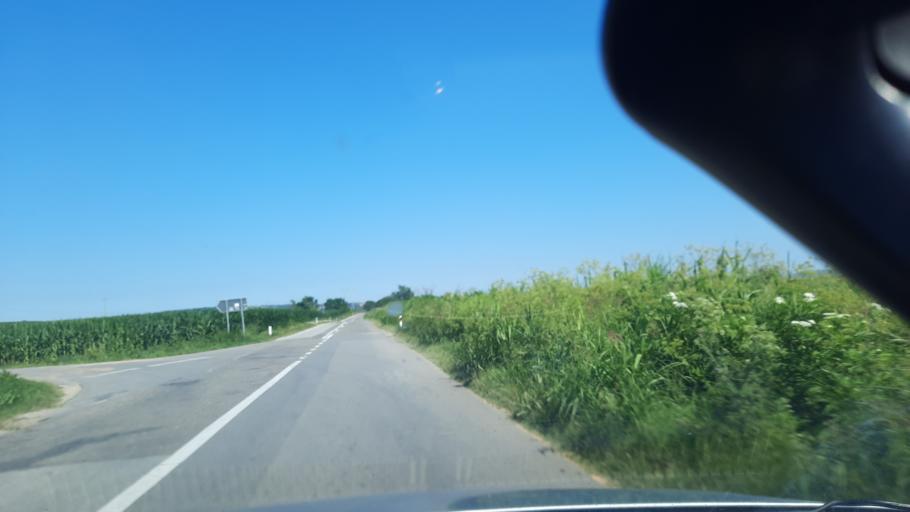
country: RS
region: Central Serbia
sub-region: Branicevski Okrug
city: Malo Crnice
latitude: 44.5803
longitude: 21.3211
